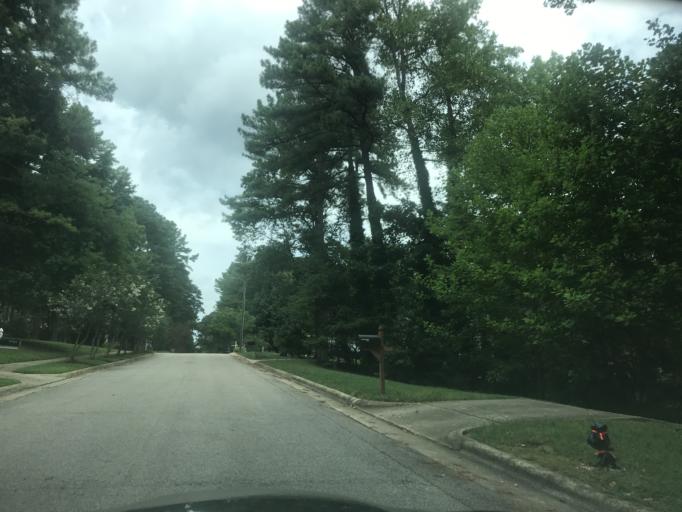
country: US
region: North Carolina
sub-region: Wake County
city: West Raleigh
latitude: 35.8889
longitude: -78.6148
